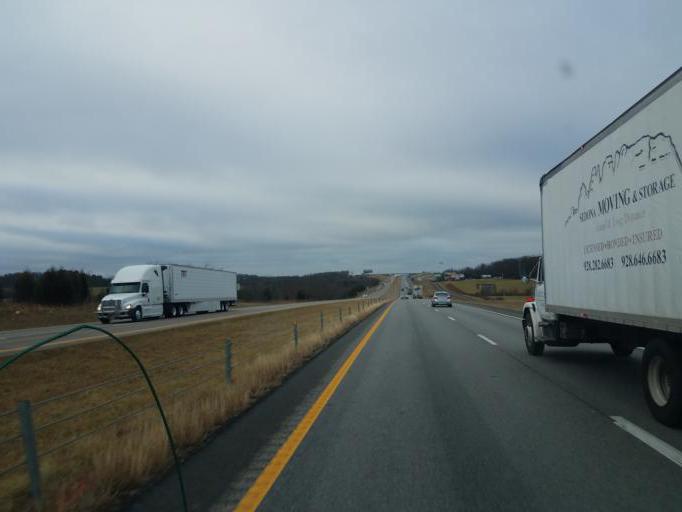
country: US
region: Missouri
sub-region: Webster County
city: Marshfield
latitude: 37.5160
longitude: -92.8358
